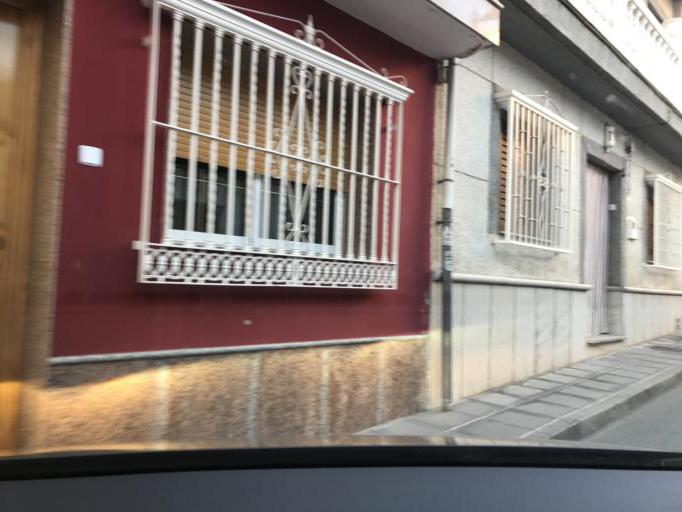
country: ES
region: Andalusia
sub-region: Provincia de Granada
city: Jun
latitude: 37.2203
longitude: -3.5936
